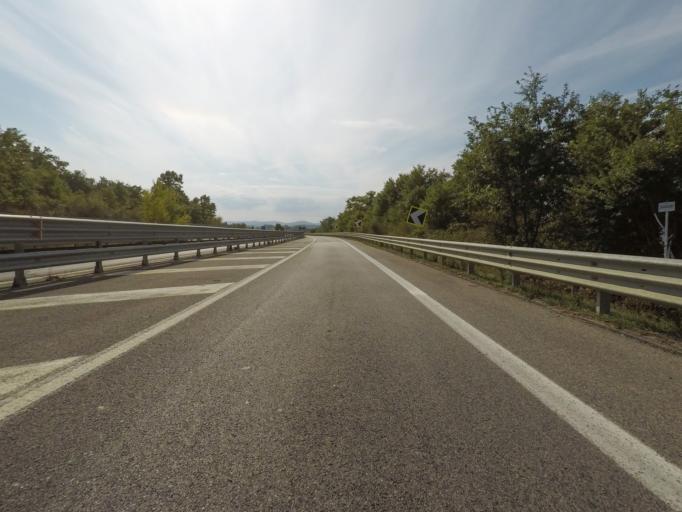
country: IT
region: Tuscany
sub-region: Provincia di Siena
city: Rosia
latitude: 43.2240
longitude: 11.2738
